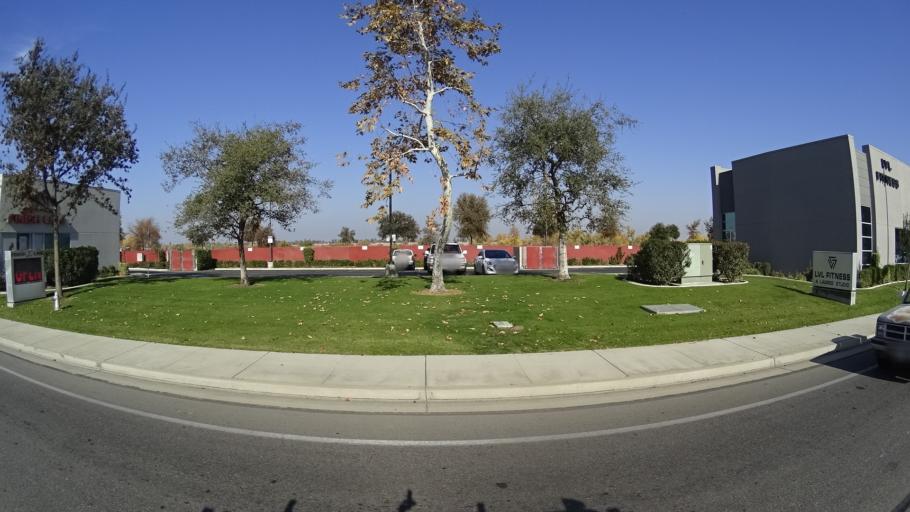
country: US
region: California
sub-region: Kern County
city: Greenacres
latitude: 35.3545
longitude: -119.1001
